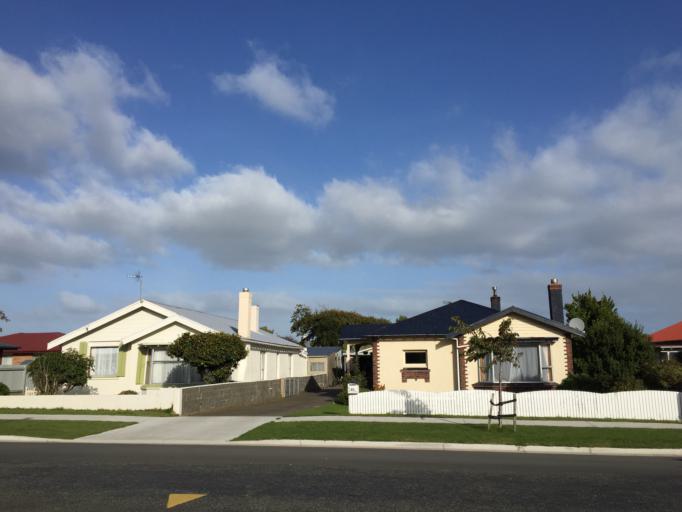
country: NZ
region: Southland
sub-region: Invercargill City
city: Invercargill
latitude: -46.4082
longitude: 168.3703
